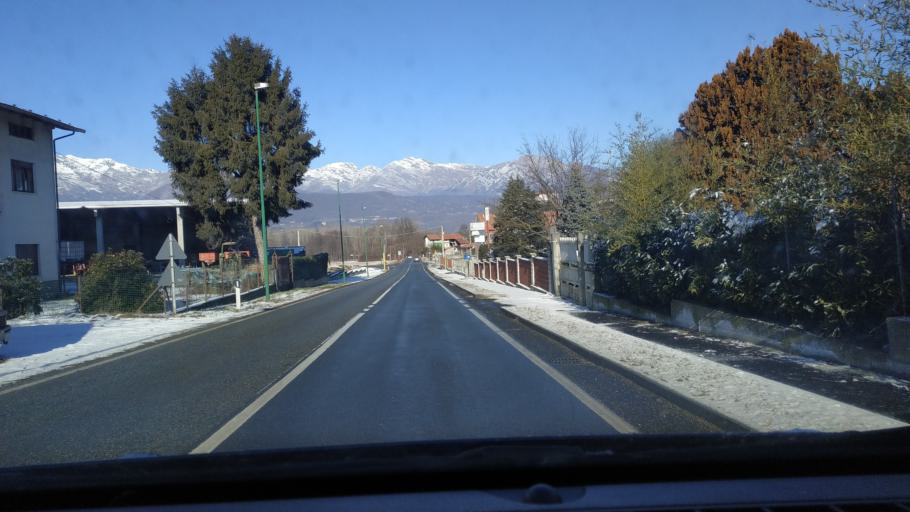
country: IT
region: Piedmont
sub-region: Provincia di Torino
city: Perosa Canavese
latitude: 45.3979
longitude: 7.8315
